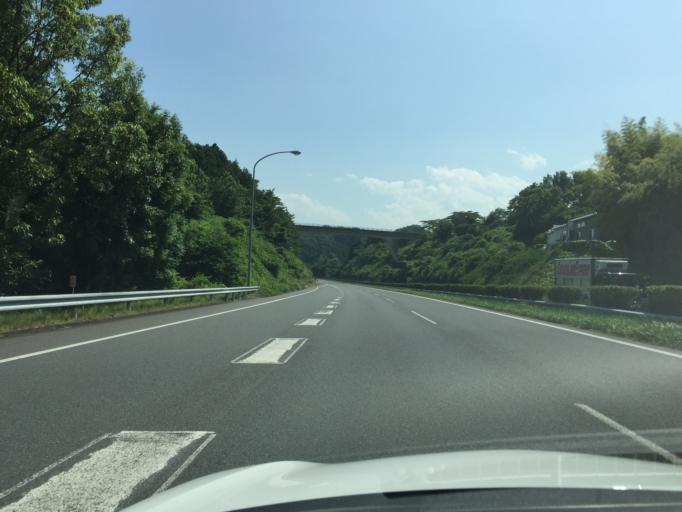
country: JP
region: Fukushima
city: Iwaki
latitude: 37.0013
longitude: 140.8085
